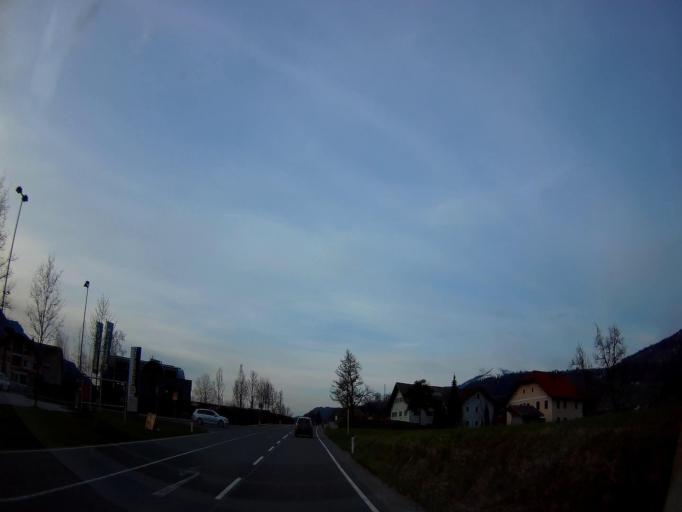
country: AT
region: Salzburg
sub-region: Politischer Bezirk Hallein
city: Golling an der Salzach
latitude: 47.6082
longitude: 13.1677
